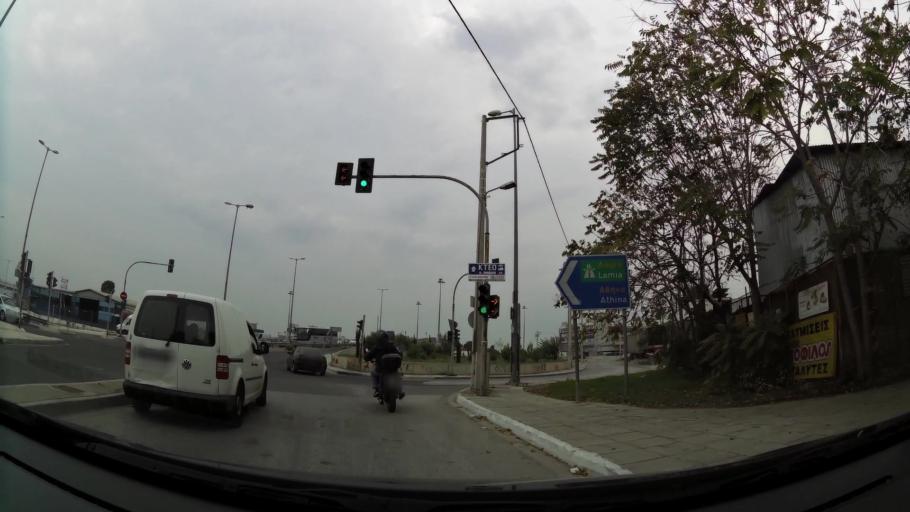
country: GR
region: Attica
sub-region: Nomarchia Athinas
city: Tavros
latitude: 37.9695
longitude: 23.6789
